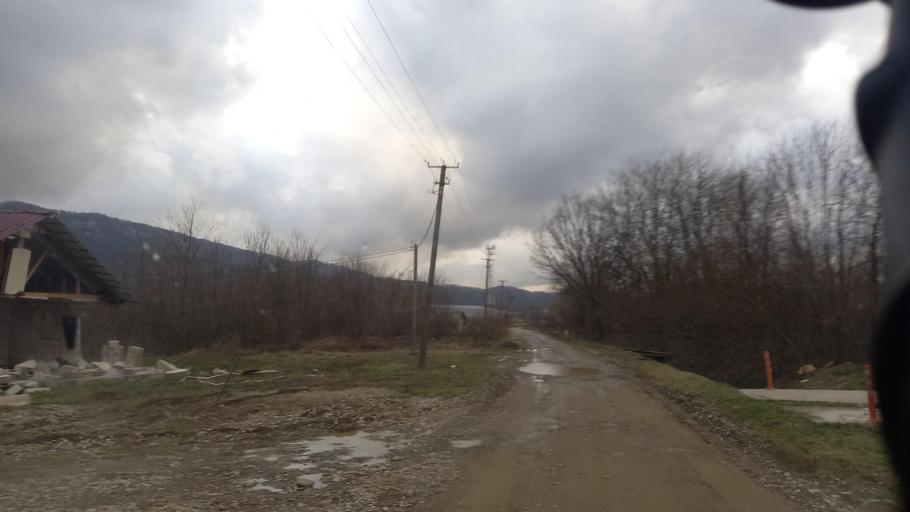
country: RU
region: Krasnodarskiy
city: Lermontovo
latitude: 44.4320
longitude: 38.7957
